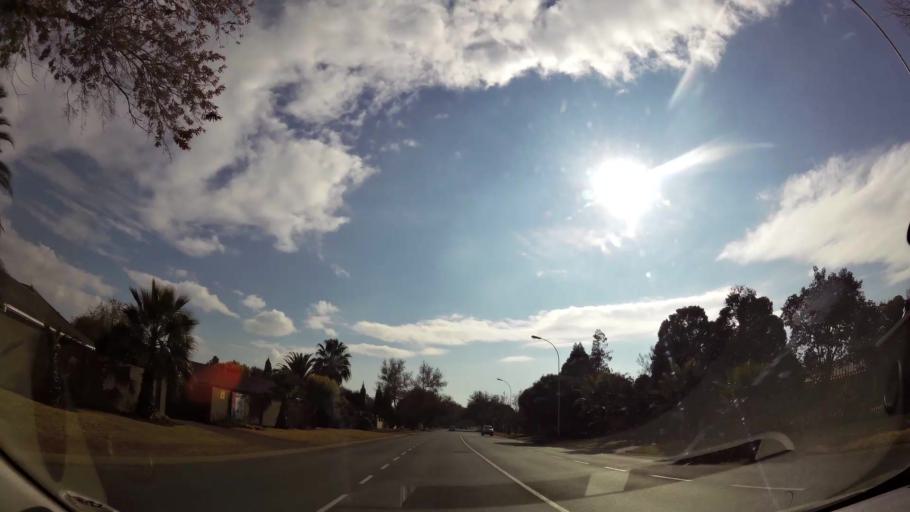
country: ZA
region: Gauteng
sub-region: Sedibeng District Municipality
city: Meyerton
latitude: -26.5539
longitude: 28.0322
